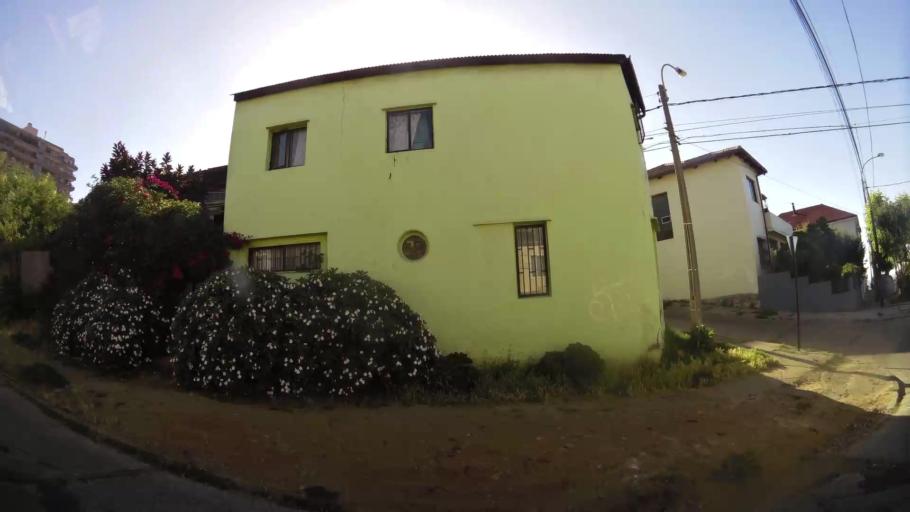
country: CL
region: Valparaiso
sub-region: Provincia de Valparaiso
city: Vina del Mar
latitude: -33.0285
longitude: -71.5687
